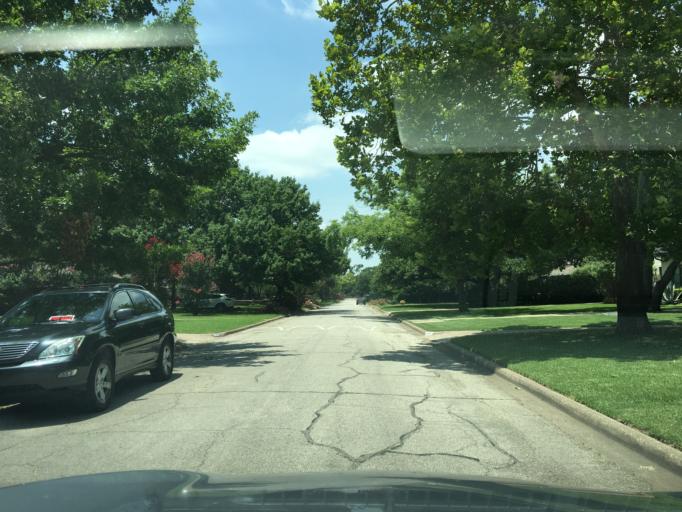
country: US
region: Texas
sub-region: Dallas County
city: Addison
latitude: 32.9175
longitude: -96.8072
